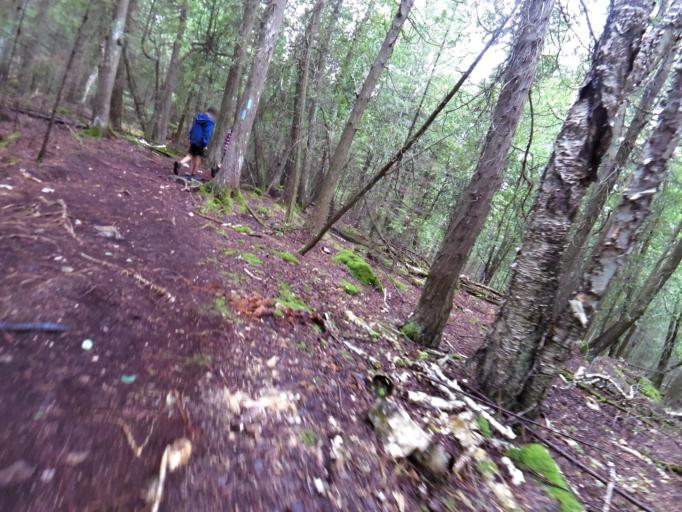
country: CA
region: Ontario
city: Tobermory
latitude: 45.2617
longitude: -81.6437
